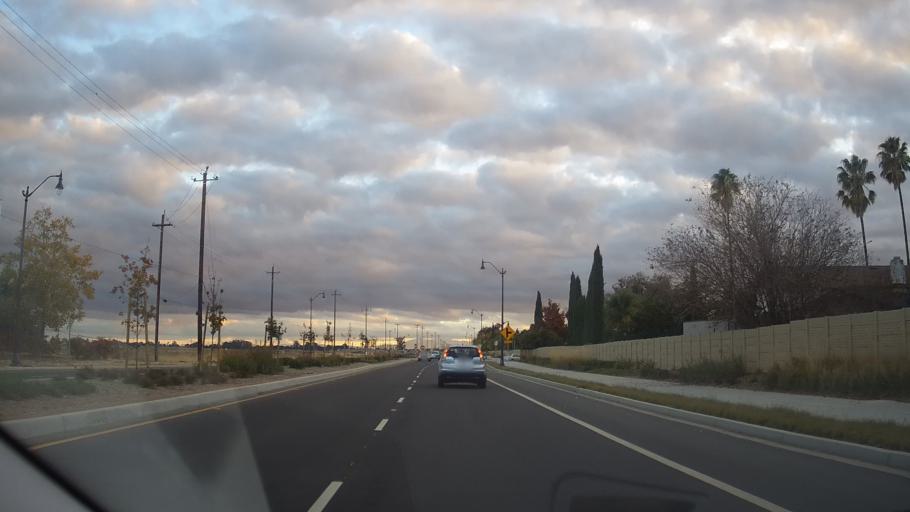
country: US
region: California
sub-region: Solano County
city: Vacaville
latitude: 38.3499
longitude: -121.9340
